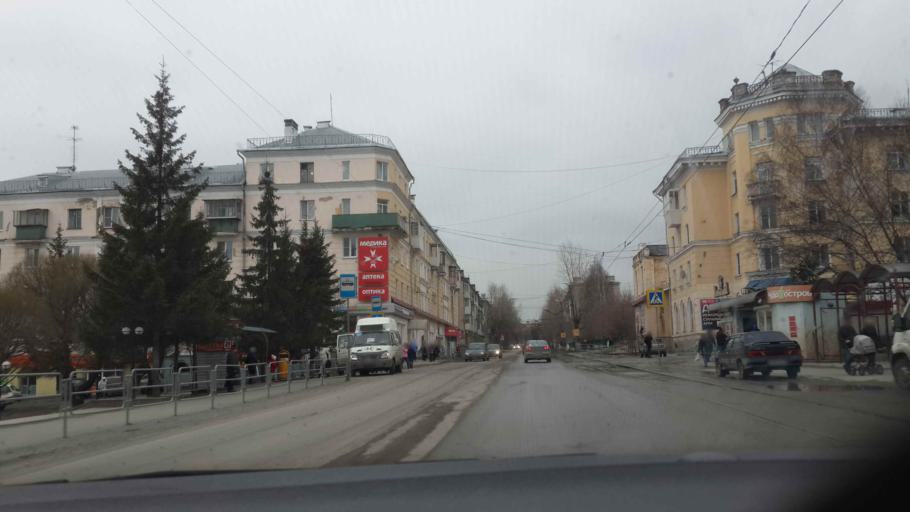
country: RU
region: Chelyabinsk
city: Zlatoust
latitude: 55.1995
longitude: 59.7170
